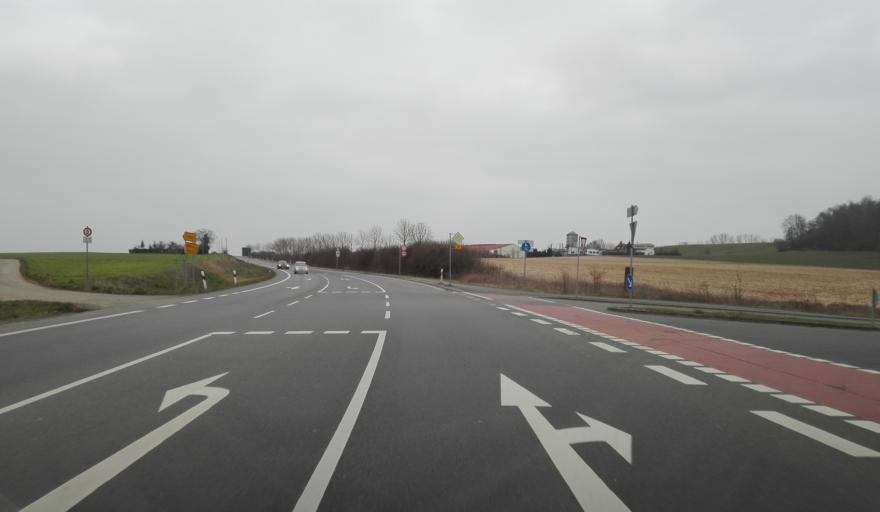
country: DE
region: Hesse
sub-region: Regierungsbezirk Darmstadt
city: Rossdorf
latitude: 49.8592
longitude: 8.7742
